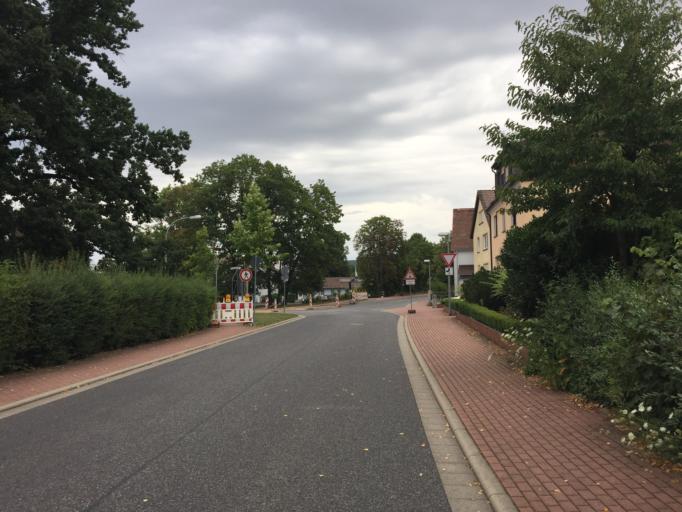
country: DE
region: Hesse
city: Bebra
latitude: 50.9758
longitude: 9.7853
